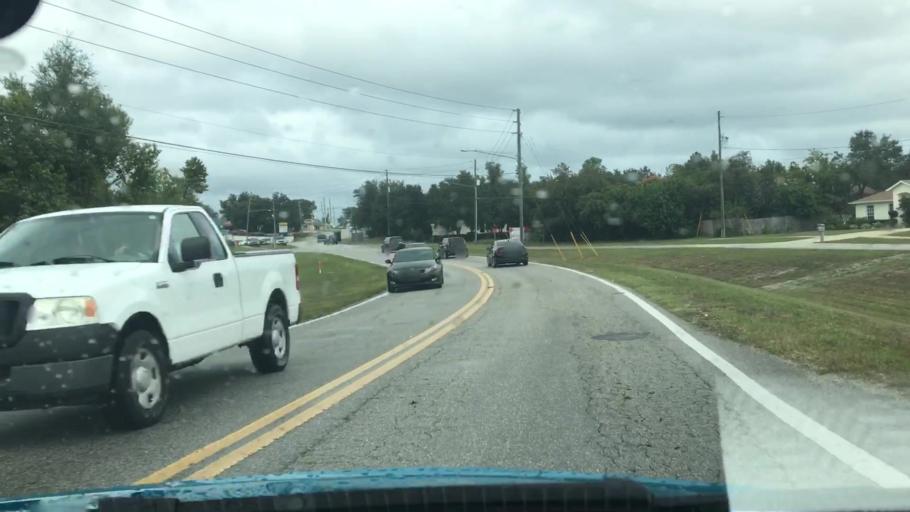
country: US
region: Florida
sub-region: Volusia County
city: Deltona
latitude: 28.9142
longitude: -81.2209
